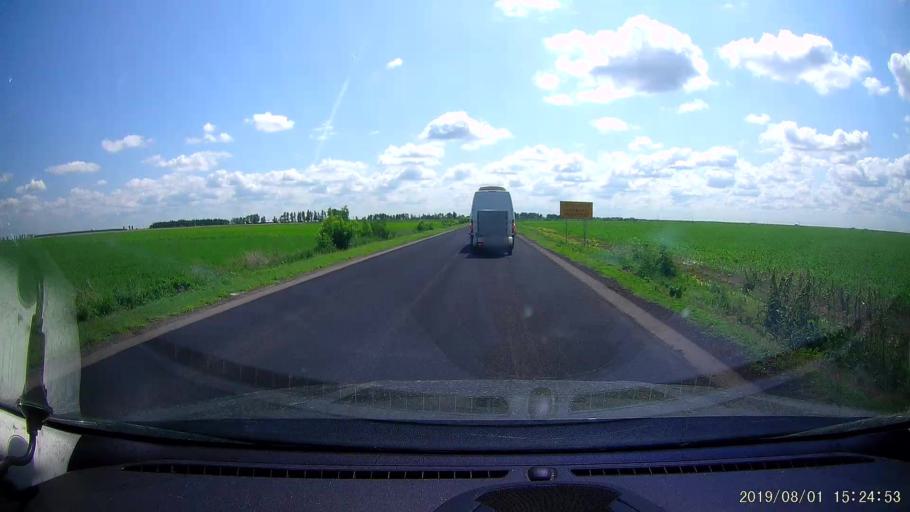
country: RO
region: Braila
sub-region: Comuna Viziru
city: Lanurile
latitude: 45.0286
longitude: 27.7434
